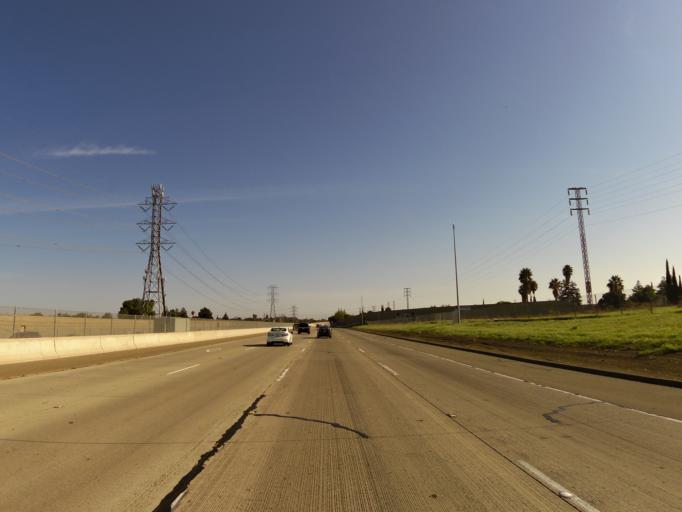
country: US
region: California
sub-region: Contra Costa County
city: Pittsburg
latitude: 38.0199
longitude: -121.9191
